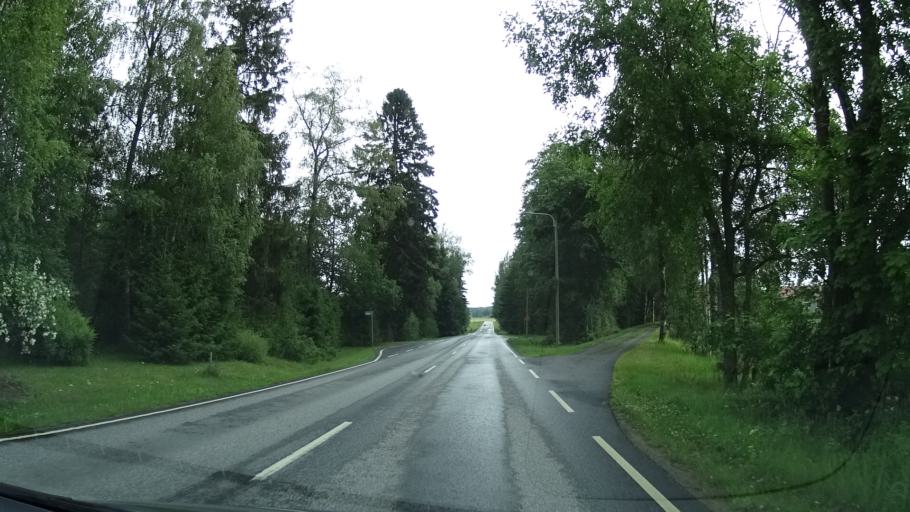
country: FI
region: Haeme
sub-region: Forssa
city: Humppila
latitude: 61.1012
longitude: 23.2884
